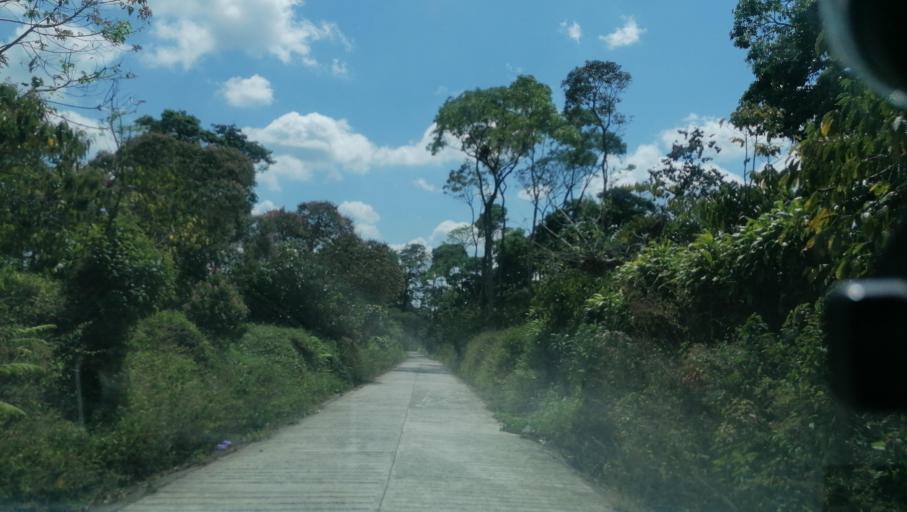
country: MX
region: Chiapas
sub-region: Union Juarez
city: Santo Domingo
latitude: 15.0396
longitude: -92.1441
